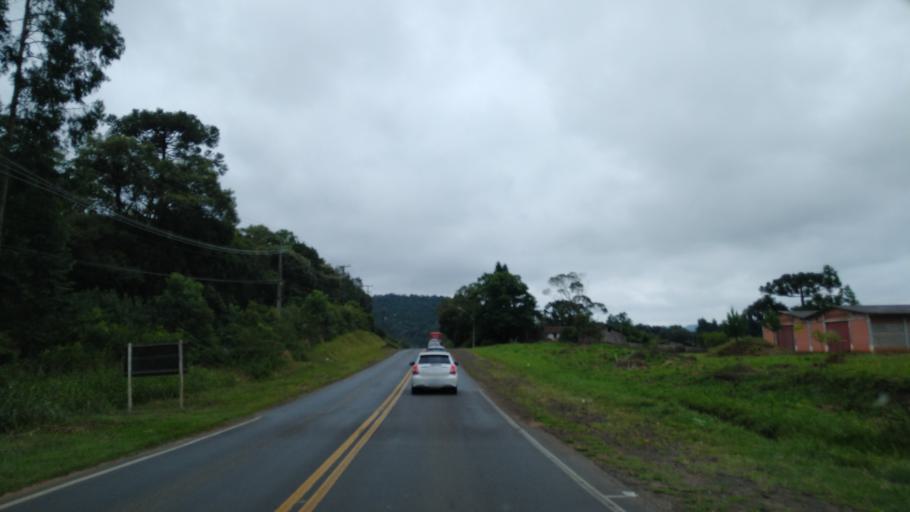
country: BR
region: Parana
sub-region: Uniao Da Vitoria
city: Uniao da Vitoria
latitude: -26.2390
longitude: -51.1245
